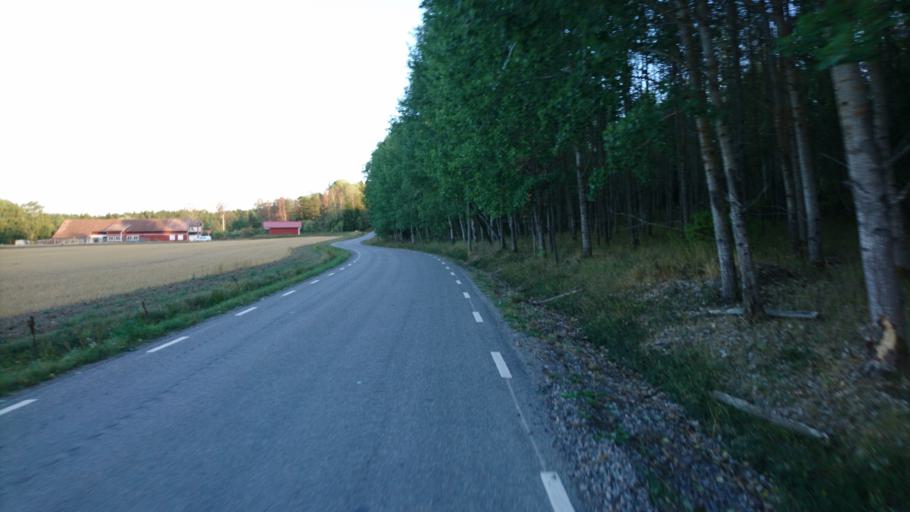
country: SE
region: Soedermanland
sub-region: Strangnas Kommun
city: Stallarholmen
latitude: 59.3977
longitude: 17.2647
